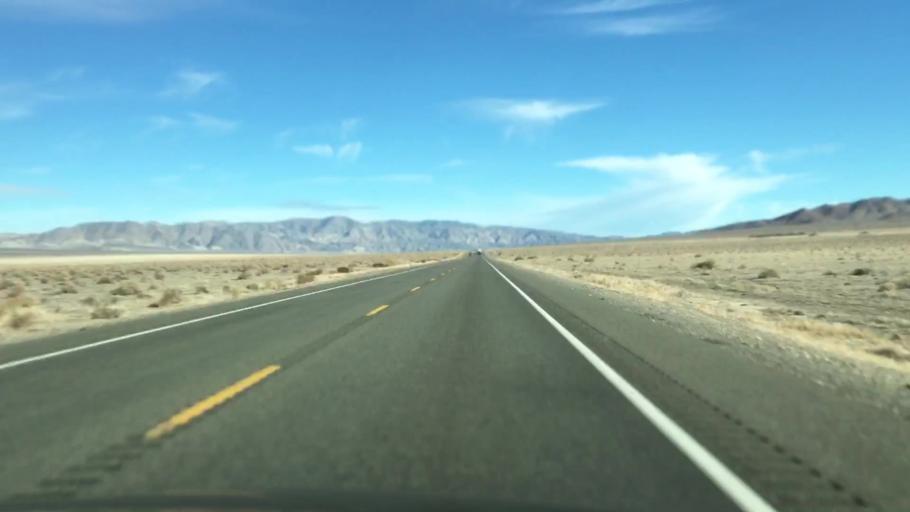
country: US
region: Nevada
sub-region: Mineral County
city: Hawthorne
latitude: 38.5374
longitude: -118.3390
